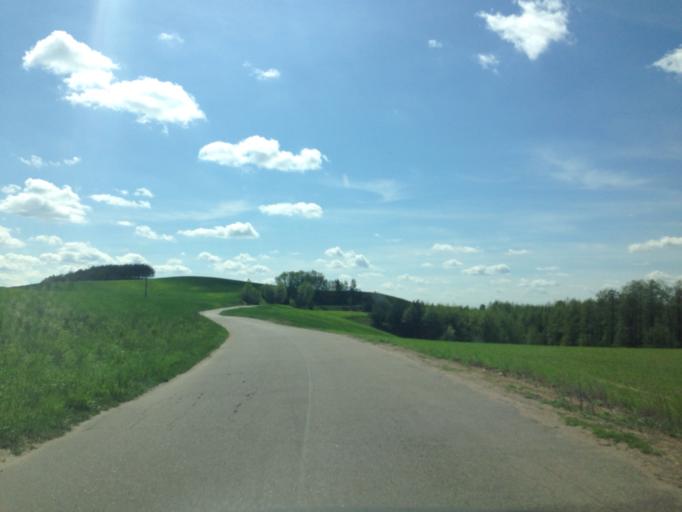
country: PL
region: Kujawsko-Pomorskie
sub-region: Powiat brodnicki
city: Bartniczka
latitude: 53.2793
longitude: 19.6520
